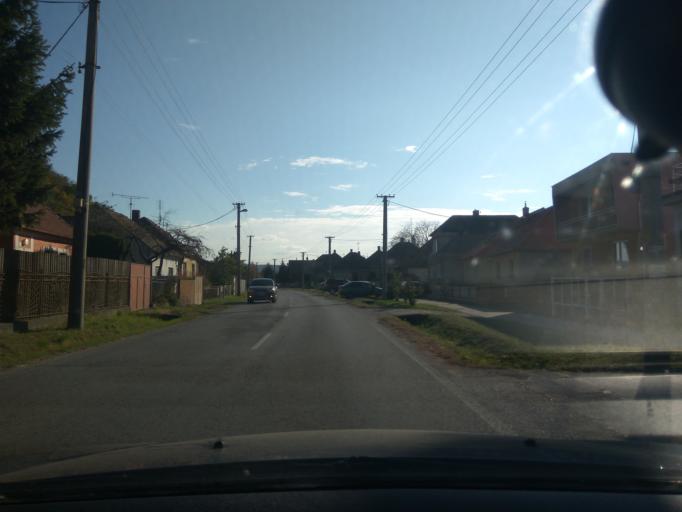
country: SK
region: Trnavsky
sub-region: Okres Trnava
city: Piestany
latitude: 48.5592
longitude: 17.8374
